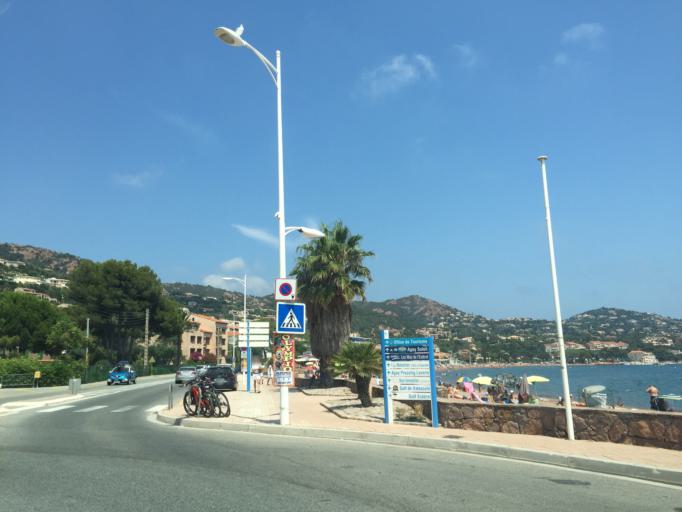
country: FR
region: Provence-Alpes-Cote d'Azur
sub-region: Departement du Var
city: Saint-Raphael
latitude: 43.4335
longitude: 6.8592
